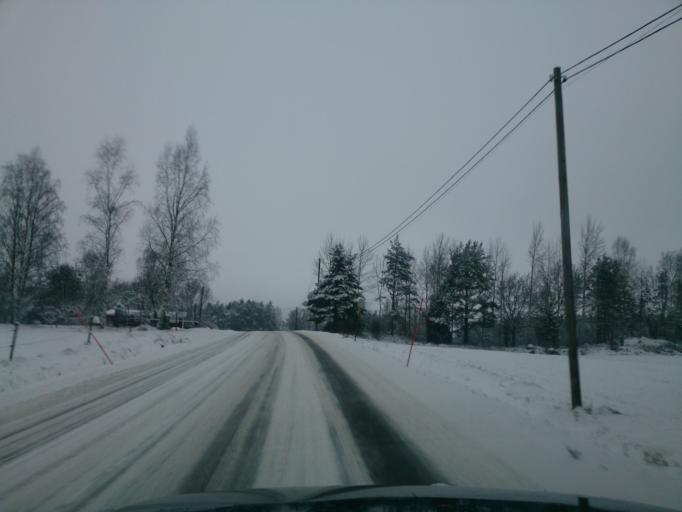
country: SE
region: OEstergoetland
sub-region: Norrkopings Kommun
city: Kimstad
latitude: 58.3887
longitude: 15.9916
